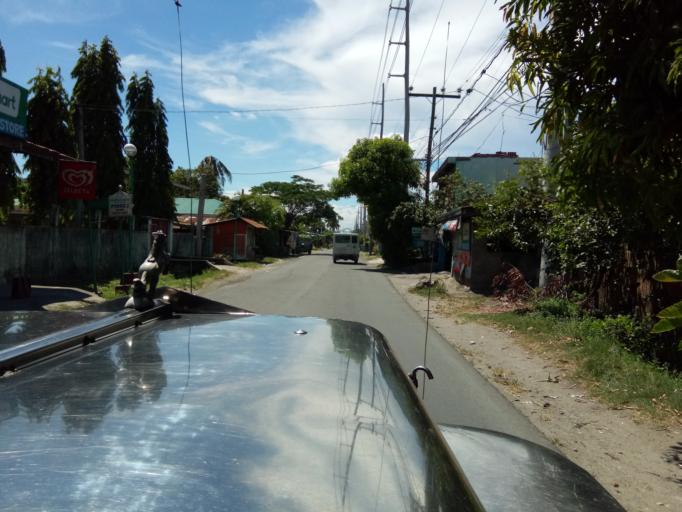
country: PH
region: Calabarzon
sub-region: Province of Cavite
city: Pasong Kawayan Primero
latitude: 14.3604
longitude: 120.8966
